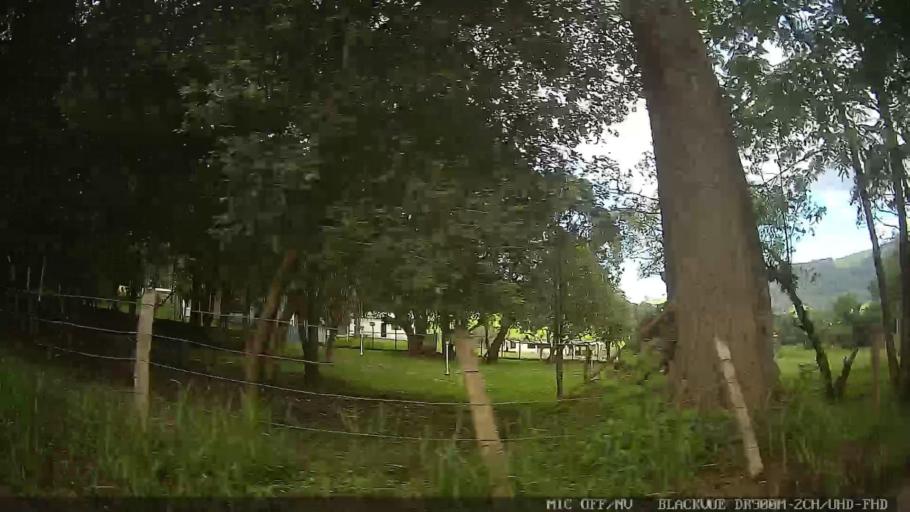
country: BR
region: Minas Gerais
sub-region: Extrema
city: Extrema
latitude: -22.8470
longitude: -46.2535
